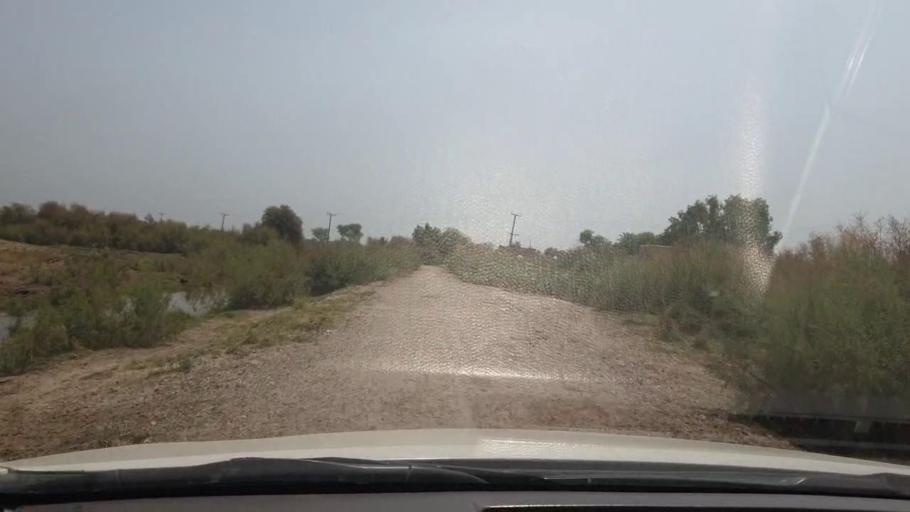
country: PK
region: Sindh
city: Shikarpur
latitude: 28.0300
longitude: 68.6489
